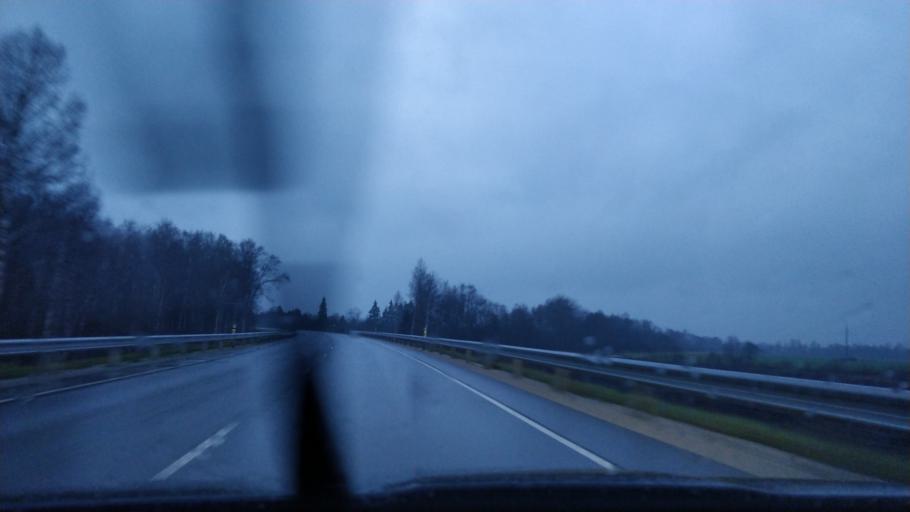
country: EE
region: Laeaene
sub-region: Lihula vald
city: Lihula
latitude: 58.7772
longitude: 23.9925
